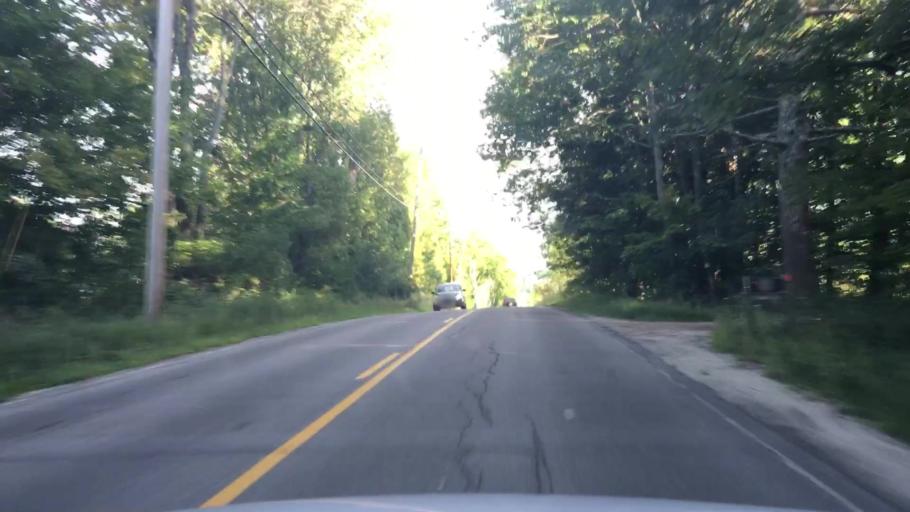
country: US
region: Maine
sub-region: Cumberland County
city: South Windham
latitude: 43.7344
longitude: -70.4144
